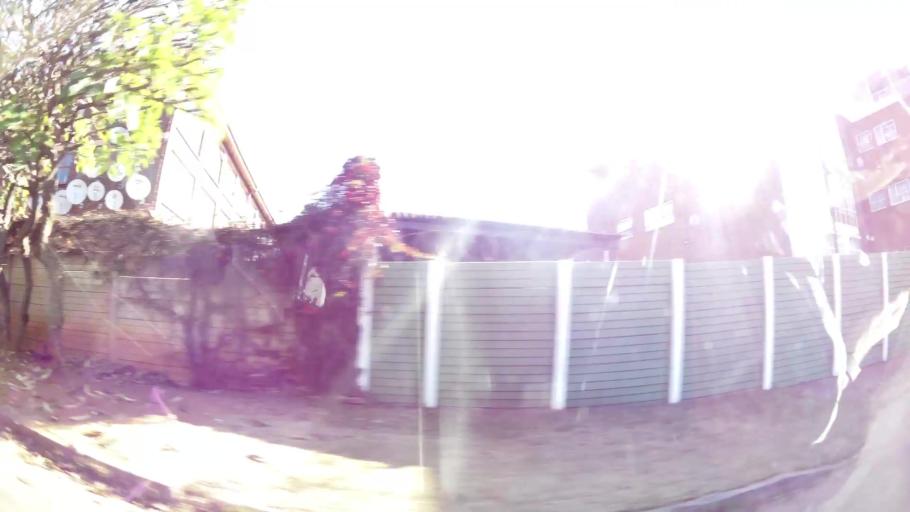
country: ZA
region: Gauteng
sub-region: City of Tshwane Metropolitan Municipality
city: Pretoria
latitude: -25.6797
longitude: 28.1712
